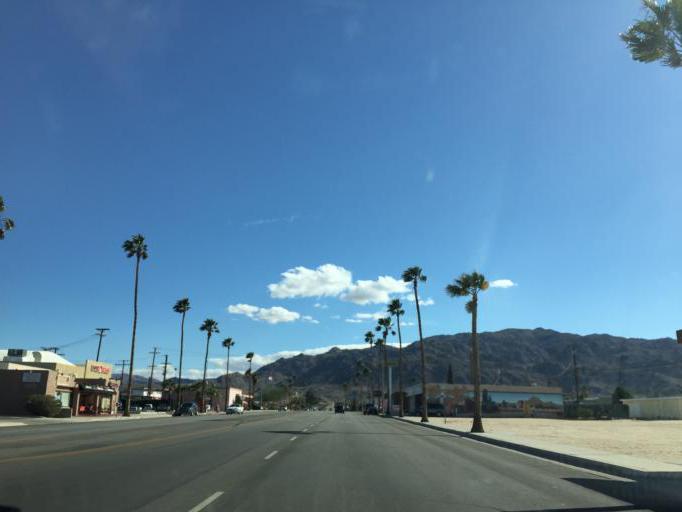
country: US
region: California
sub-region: San Bernardino County
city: Twentynine Palms
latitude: 34.1393
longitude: -116.0545
